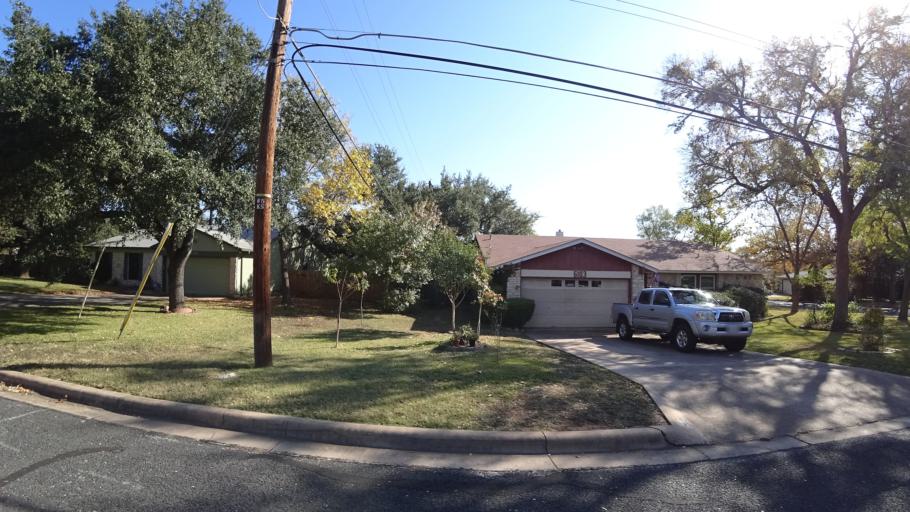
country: US
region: Texas
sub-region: Travis County
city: Barton Creek
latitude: 30.2330
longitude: -97.8495
